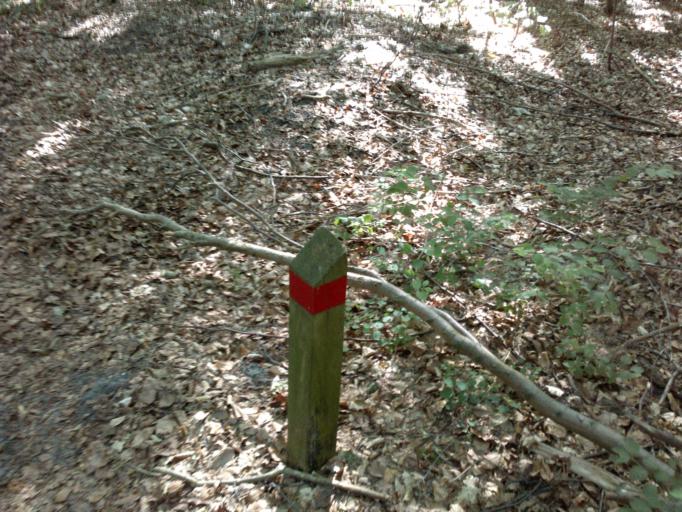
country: NL
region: South Holland
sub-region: Gemeente Hellevoetsluis
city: Nieuw-Helvoet
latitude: 51.8966
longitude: 4.0653
